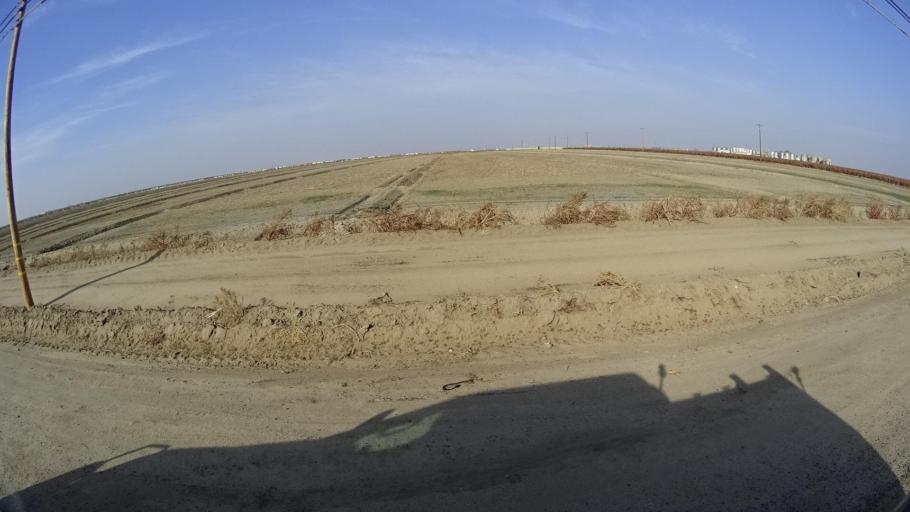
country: US
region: California
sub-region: Kern County
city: Delano
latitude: 35.7760
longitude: -119.1973
